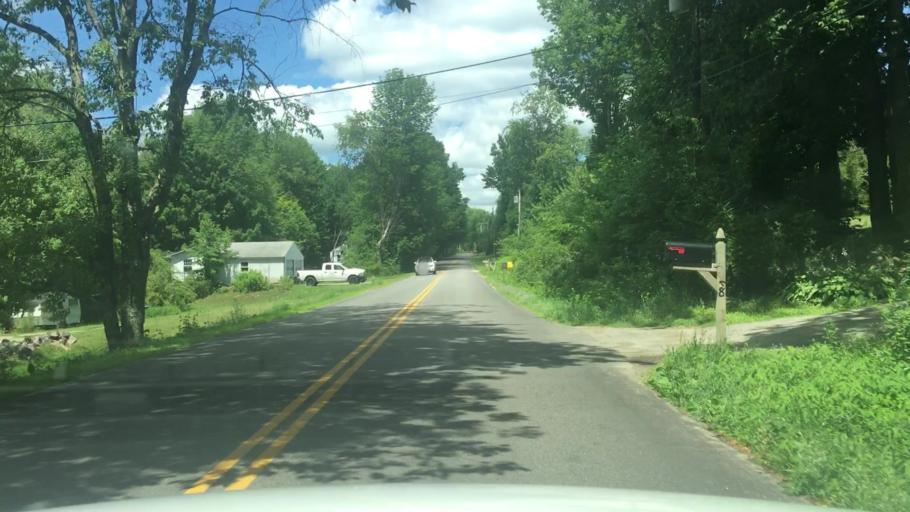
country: US
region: Maine
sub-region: Waldo County
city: Belfast
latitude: 44.4142
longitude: -69.0401
